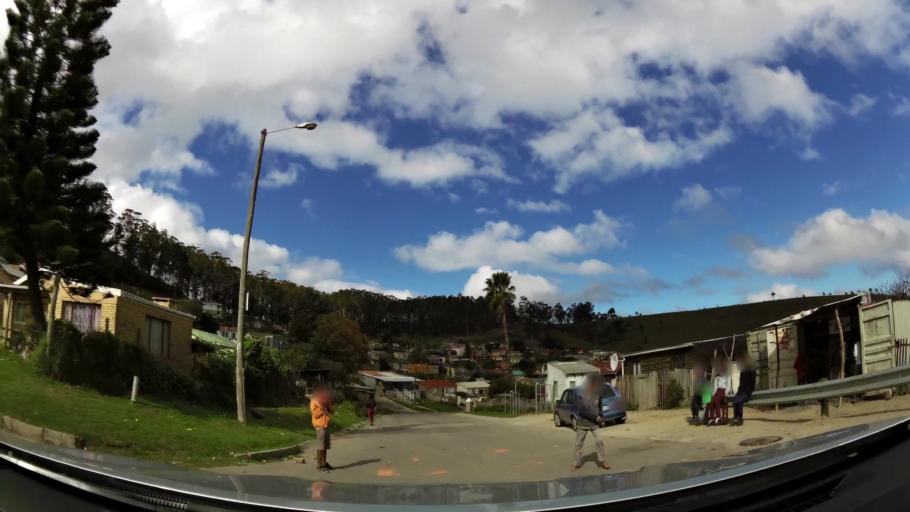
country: ZA
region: Western Cape
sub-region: Eden District Municipality
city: Knysna
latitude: -34.0517
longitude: 23.1054
